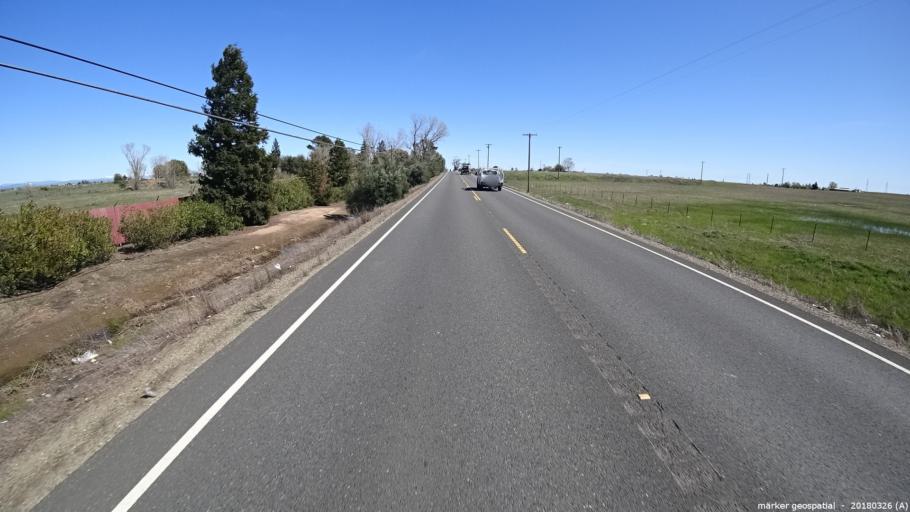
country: US
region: California
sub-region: Sacramento County
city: Rosemont
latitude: 38.5236
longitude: -121.3148
